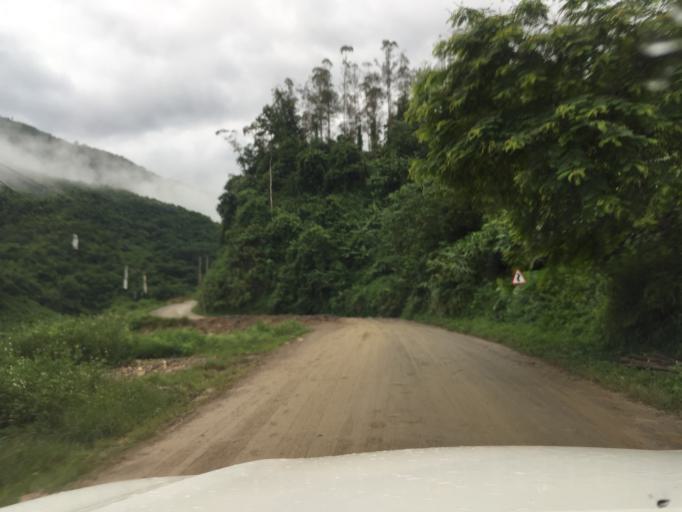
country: LA
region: Oudomxai
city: Muang La
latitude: 21.0023
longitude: 102.2325
